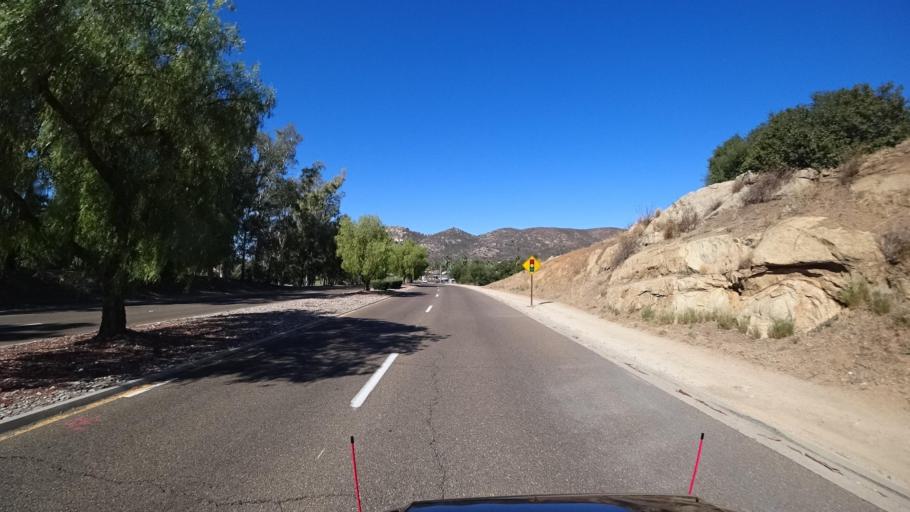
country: US
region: California
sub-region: San Diego County
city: San Diego Country Estates
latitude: 33.0057
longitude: -116.8161
